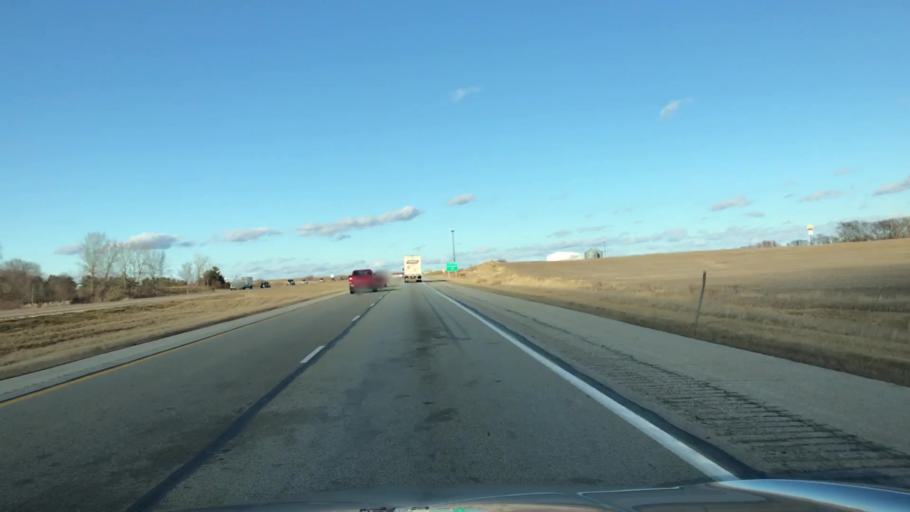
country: US
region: Illinois
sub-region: McLean County
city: Lexington
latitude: 40.6381
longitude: -88.8126
